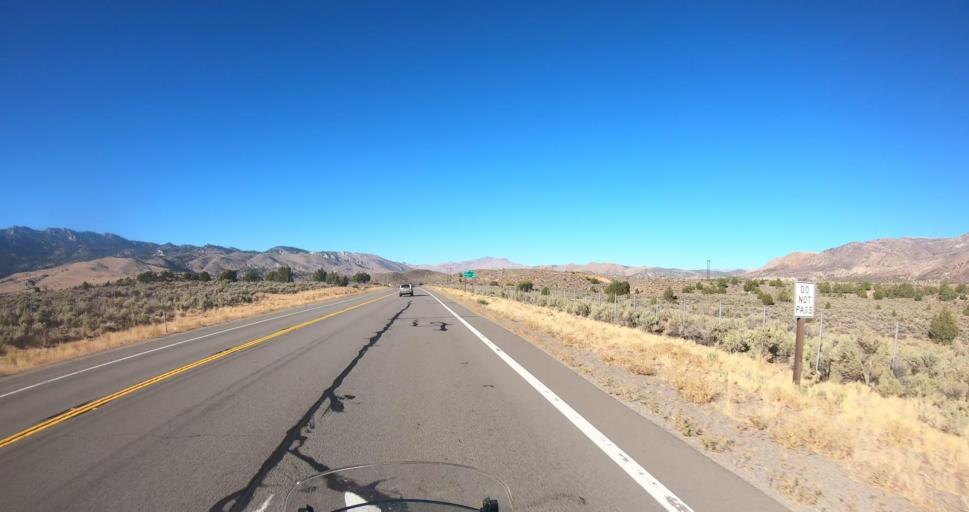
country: US
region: Nevada
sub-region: Washoe County
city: Cold Springs
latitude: 39.8546
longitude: -120.0413
